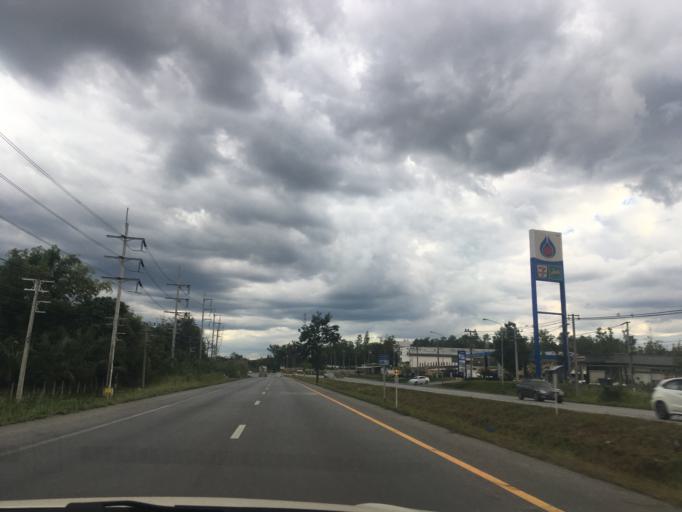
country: TH
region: Chon Buri
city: Nong Yai
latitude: 13.1643
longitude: 101.2834
